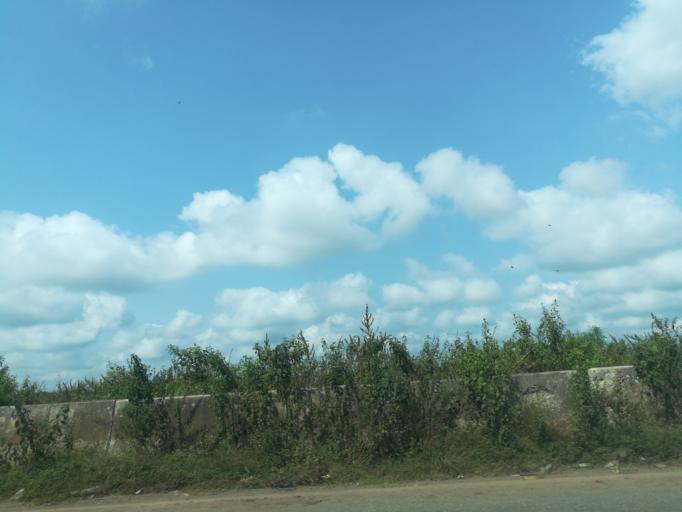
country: NG
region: Oyo
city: Moniya
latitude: 7.5367
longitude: 3.9163
